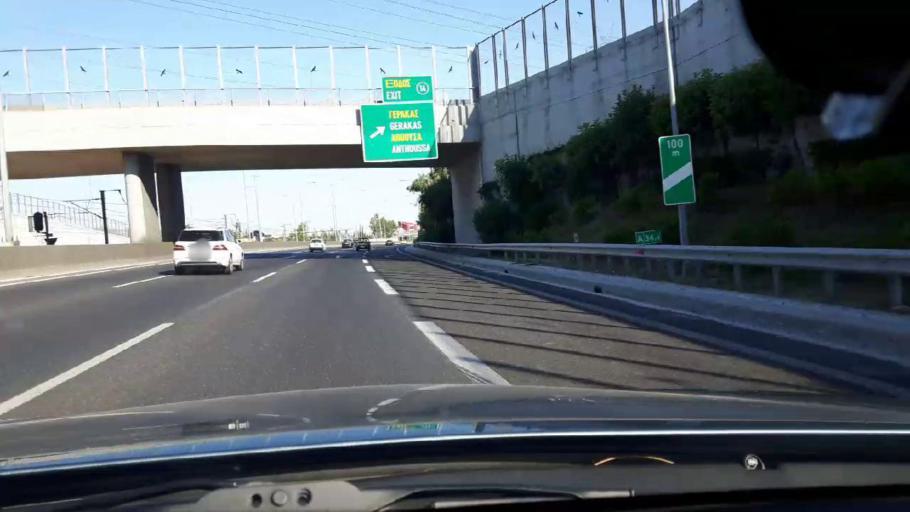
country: GR
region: Attica
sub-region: Nomarchia Anatolikis Attikis
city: Pallini
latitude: 38.0088
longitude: 23.8683
